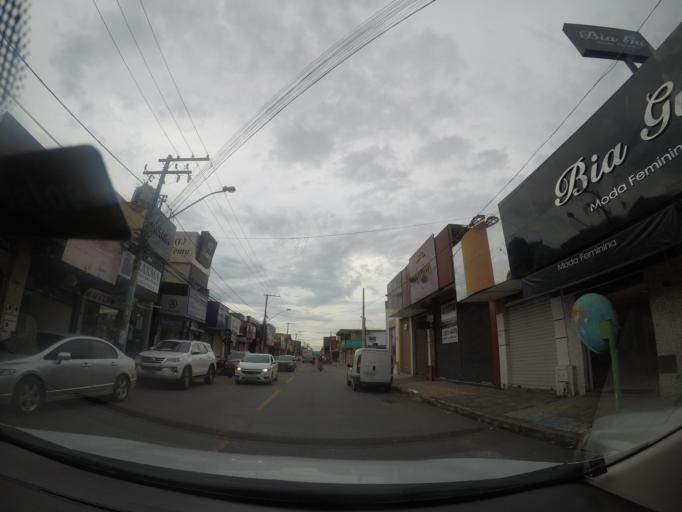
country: BR
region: Goias
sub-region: Goiania
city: Goiania
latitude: -16.6626
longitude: -49.2774
